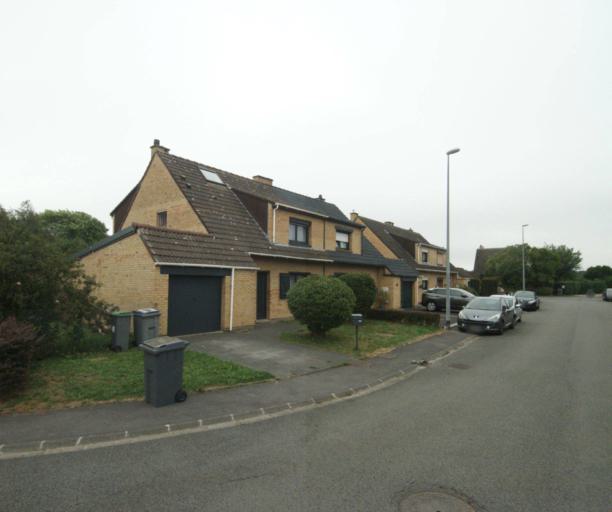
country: FR
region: Nord-Pas-de-Calais
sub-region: Departement du Nord
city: Baisieux
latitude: 50.6126
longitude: 3.2472
